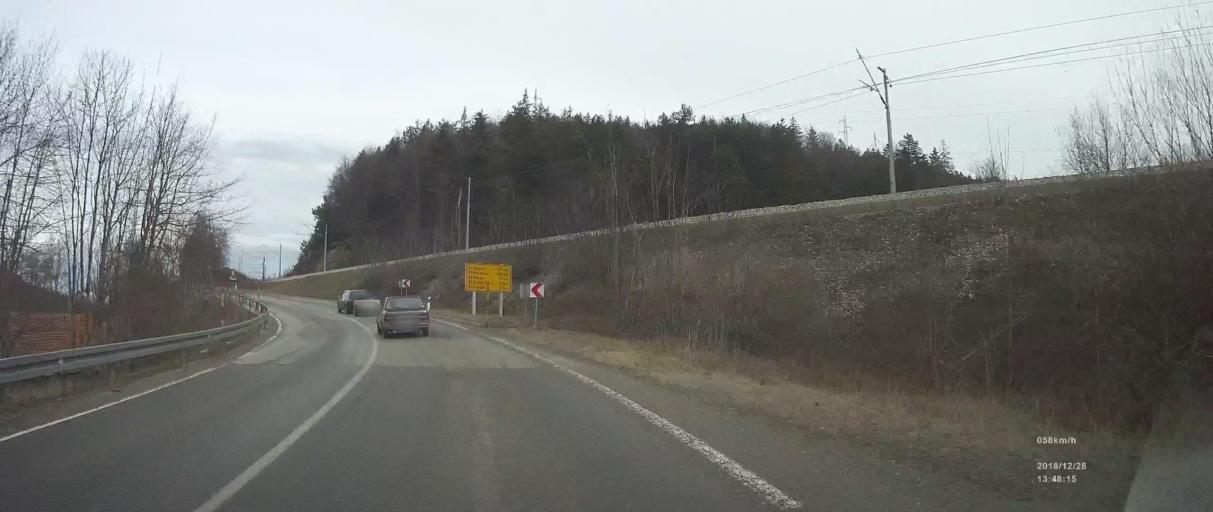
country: HR
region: Primorsko-Goranska
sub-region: Grad Delnice
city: Delnice
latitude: 45.3957
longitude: 14.8080
